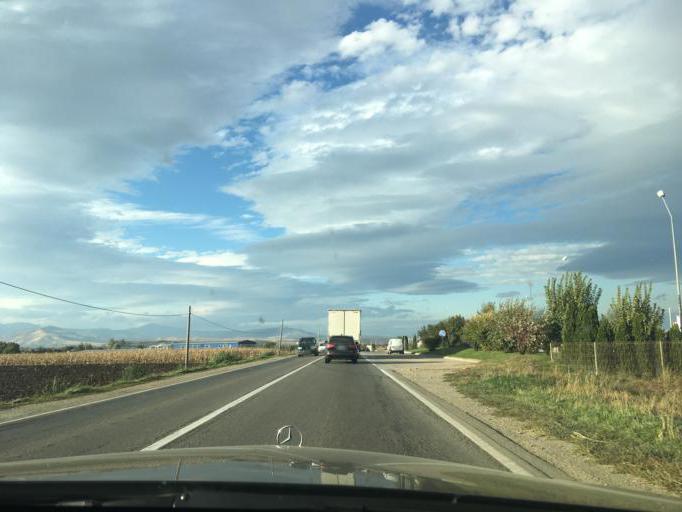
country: RO
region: Alba
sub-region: Comuna Santimbru
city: Santimbru
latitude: 46.1531
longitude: 23.6433
